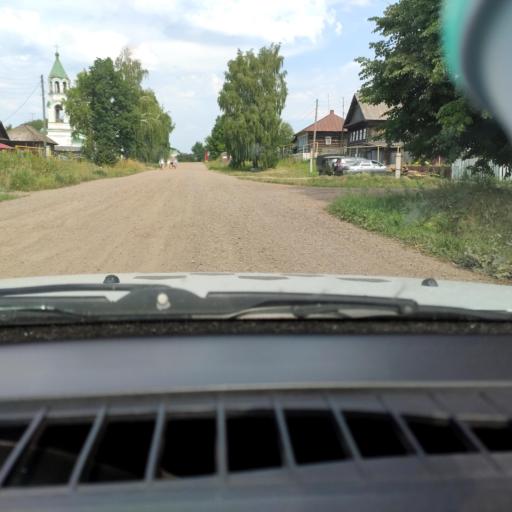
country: RU
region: Perm
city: Uinskoye
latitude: 57.1162
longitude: 56.5211
